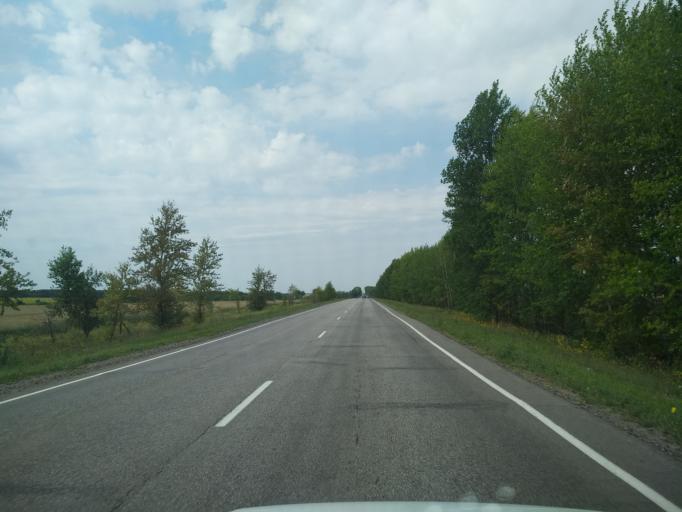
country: RU
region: Voronezj
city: Pereleshino
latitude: 51.7165
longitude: 40.0163
